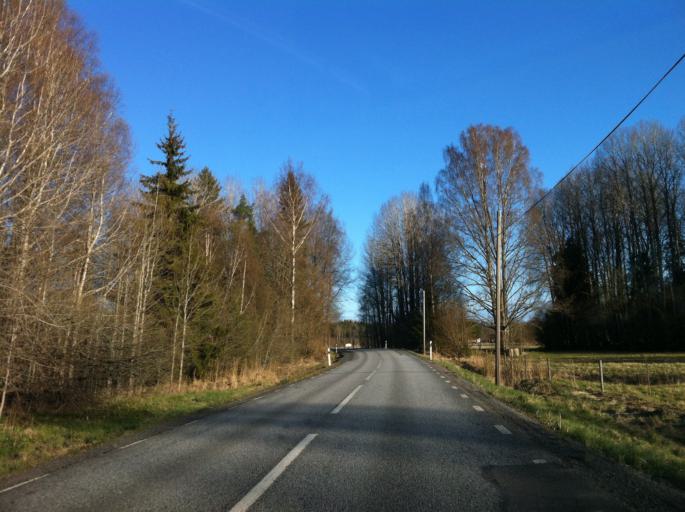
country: SE
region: Uppsala
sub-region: Osthammars Kommun
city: Anneberg
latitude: 60.1560
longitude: 18.4193
